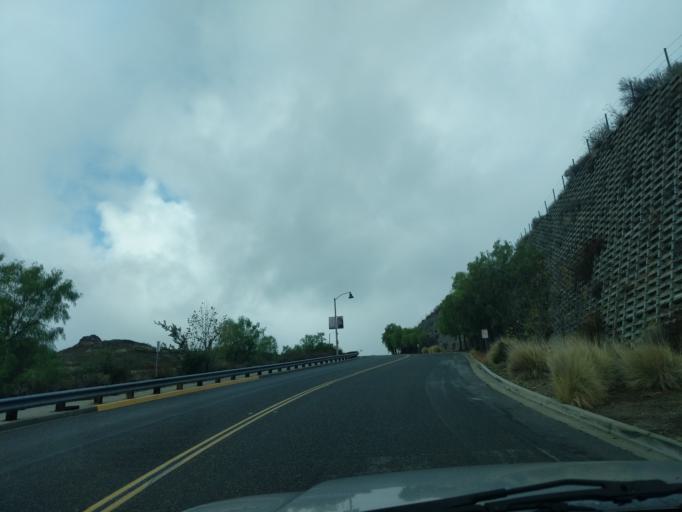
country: US
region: California
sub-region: Ventura County
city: Simi Valley
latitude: 34.2577
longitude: -118.8122
